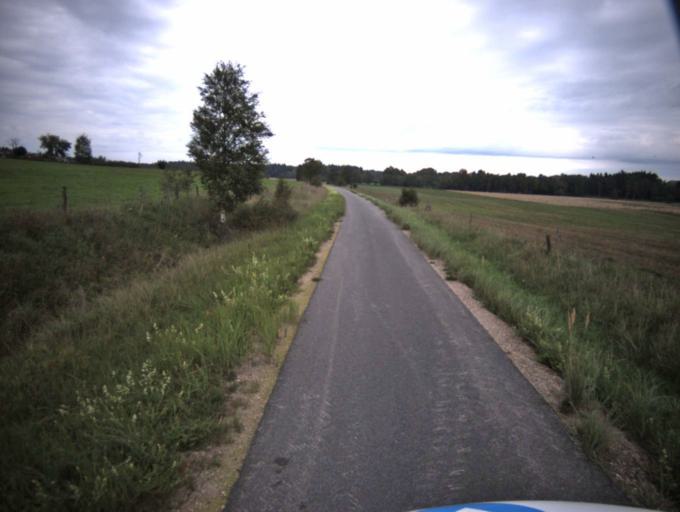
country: SE
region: Vaestra Goetaland
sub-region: Falkopings Kommun
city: Falkoeping
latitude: 57.9969
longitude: 13.5438
